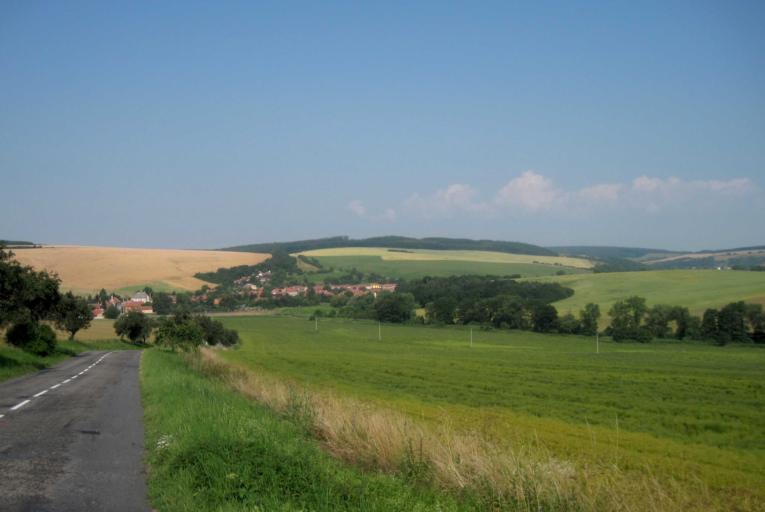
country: CZ
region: Zlin
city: Korycany
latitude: 49.1088
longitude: 17.1500
